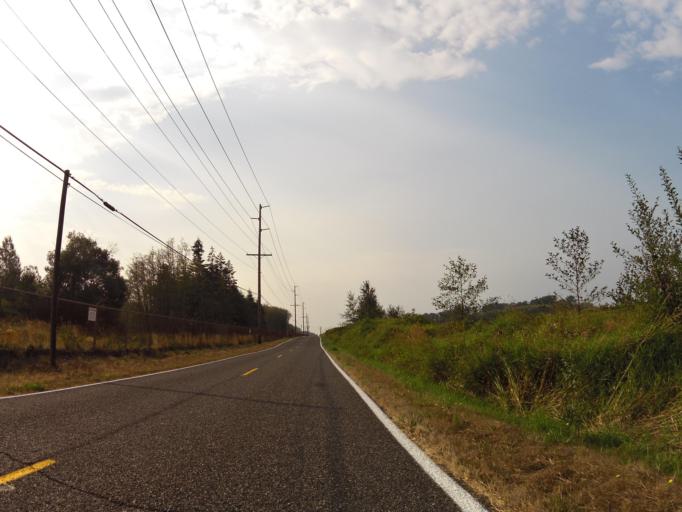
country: US
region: Washington
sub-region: Whatcom County
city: Birch Bay
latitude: 48.8823
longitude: -122.7489
